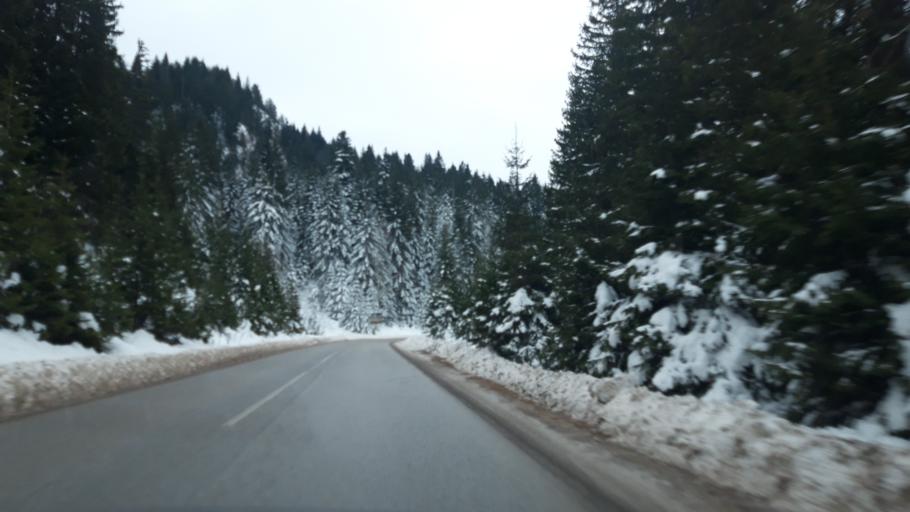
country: BA
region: Republika Srpska
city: Koran
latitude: 43.7697
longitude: 18.5486
